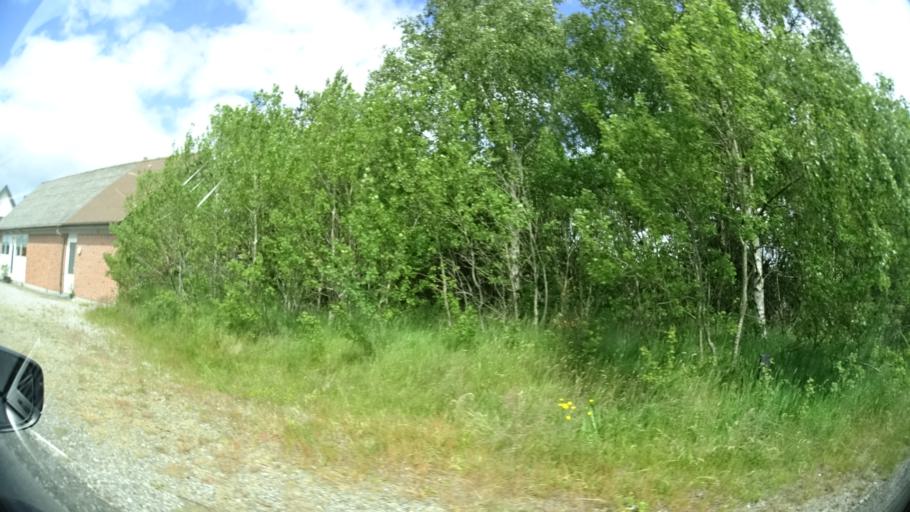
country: DK
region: Central Jutland
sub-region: Norddjurs Kommune
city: Grenaa
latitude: 56.5296
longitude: 10.7110
